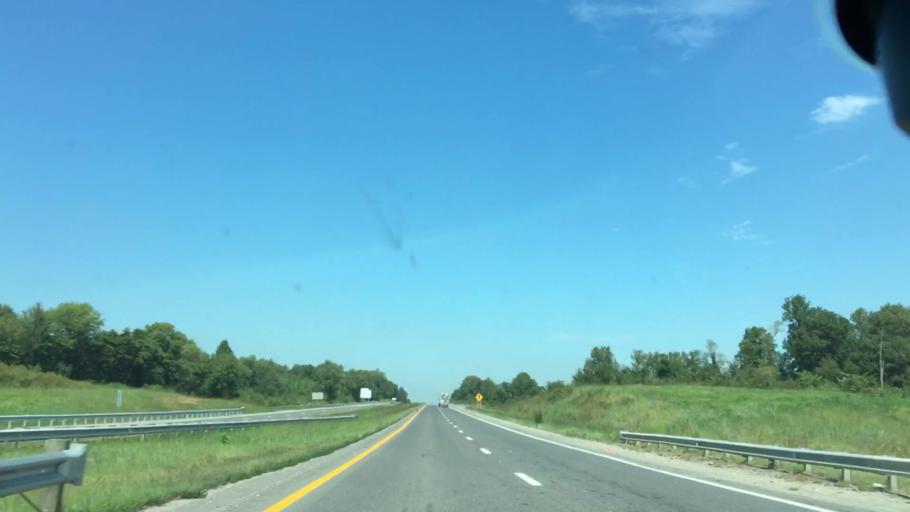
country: US
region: Kentucky
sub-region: Webster County
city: Sebree
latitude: 37.4905
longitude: -87.4754
